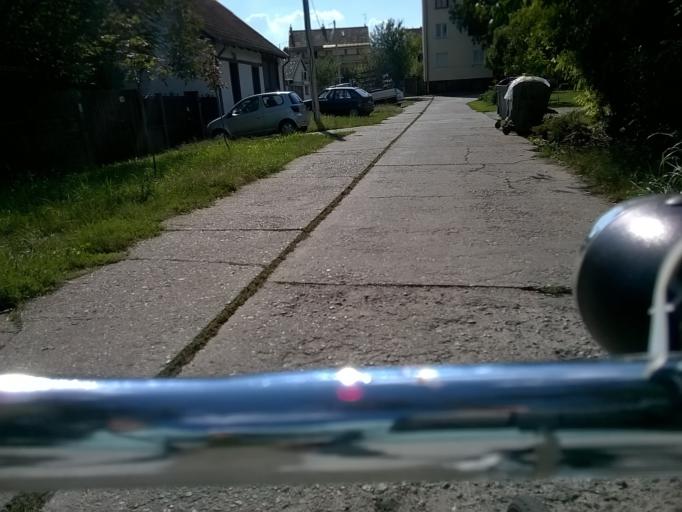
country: RS
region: Autonomna Pokrajina Vojvodina
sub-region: Juznobanatski Okrug
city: Pancevo
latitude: 44.8770
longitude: 20.6436
